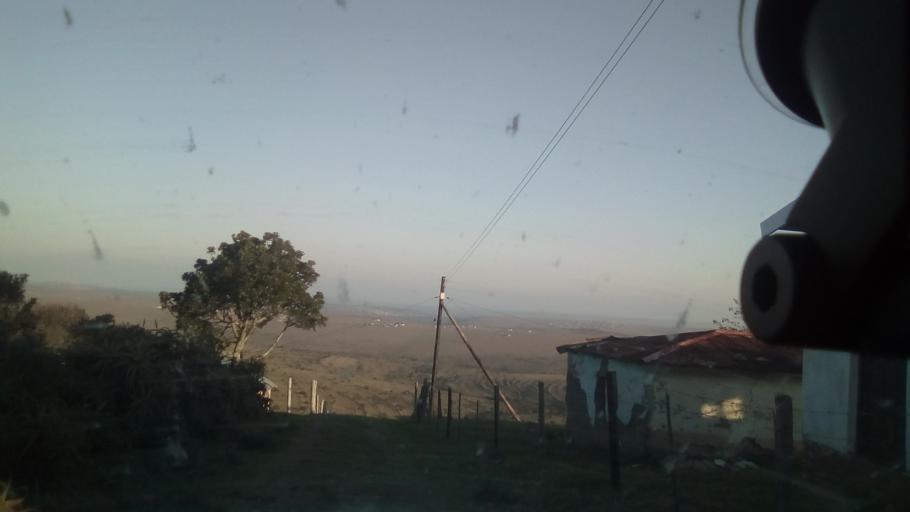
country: ZA
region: Eastern Cape
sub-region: Buffalo City Metropolitan Municipality
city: Bhisho
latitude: -32.9734
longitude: 27.2935
